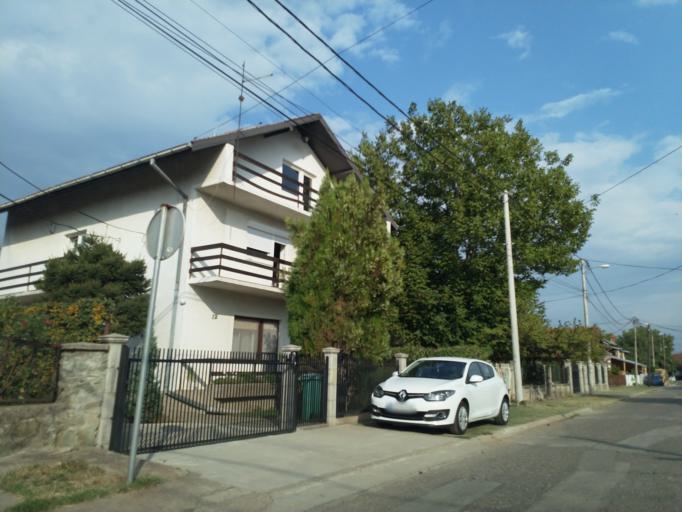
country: RS
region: Central Serbia
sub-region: Pomoravski Okrug
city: Paracin
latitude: 43.8666
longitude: 21.4116
